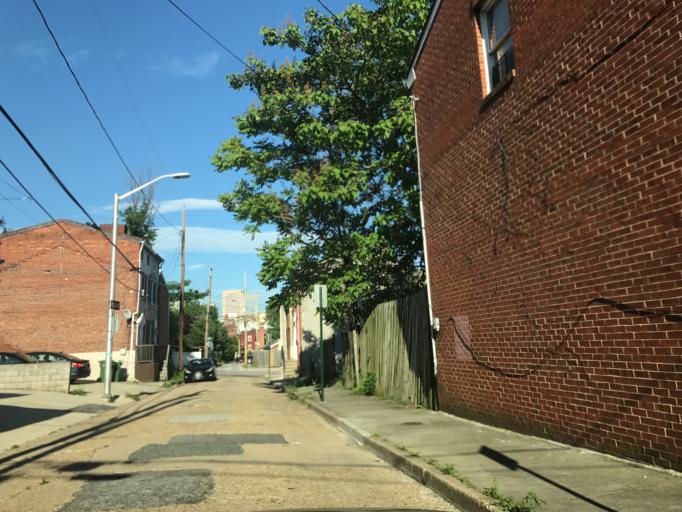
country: US
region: Maryland
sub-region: City of Baltimore
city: Baltimore
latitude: 39.2865
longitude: -76.6313
